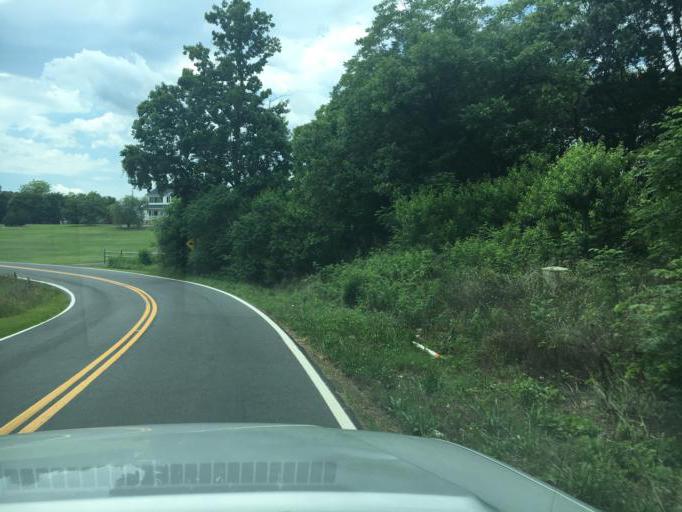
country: US
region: South Carolina
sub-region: Spartanburg County
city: Duncan
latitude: 34.8767
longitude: -82.1866
